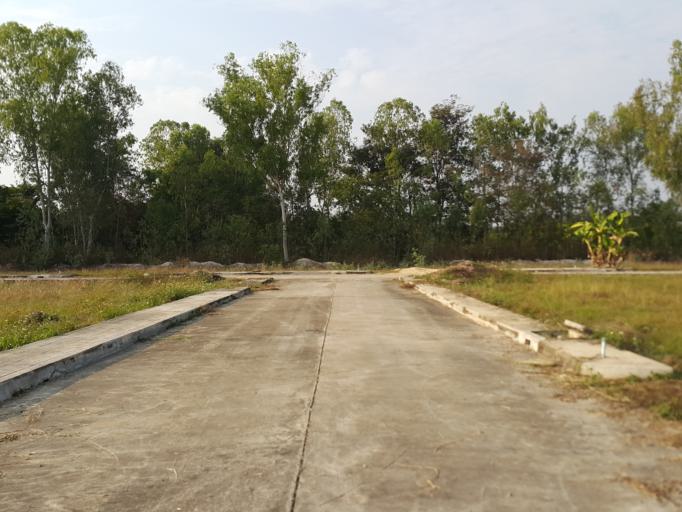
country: TH
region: Chiang Mai
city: San Sai
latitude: 18.8780
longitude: 99.1465
